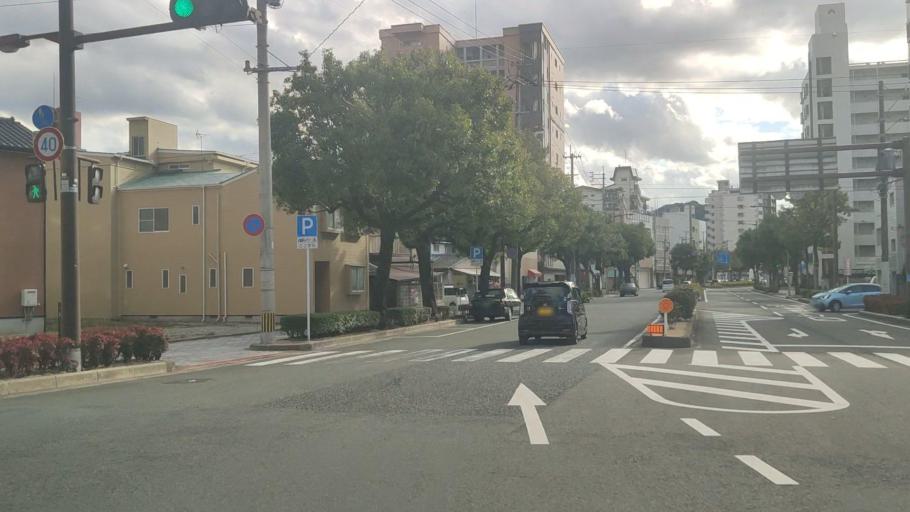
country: JP
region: Yamaguchi
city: Shimonoseki
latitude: 33.9519
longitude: 130.9673
